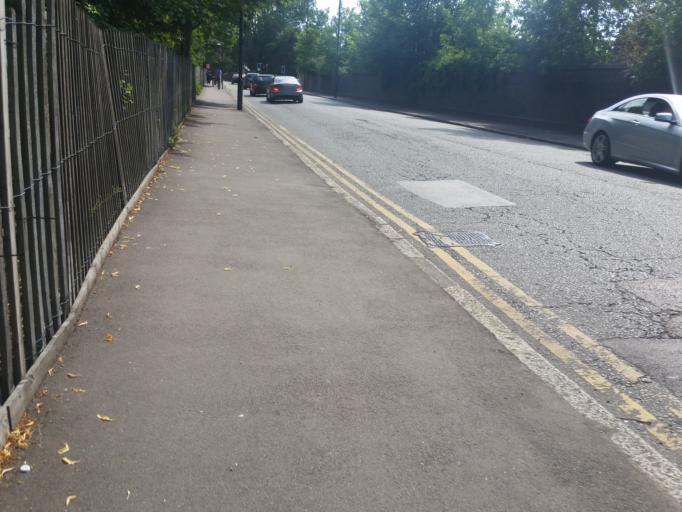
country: GB
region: England
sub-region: Greater London
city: Harringay
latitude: 51.5735
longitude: -0.1046
